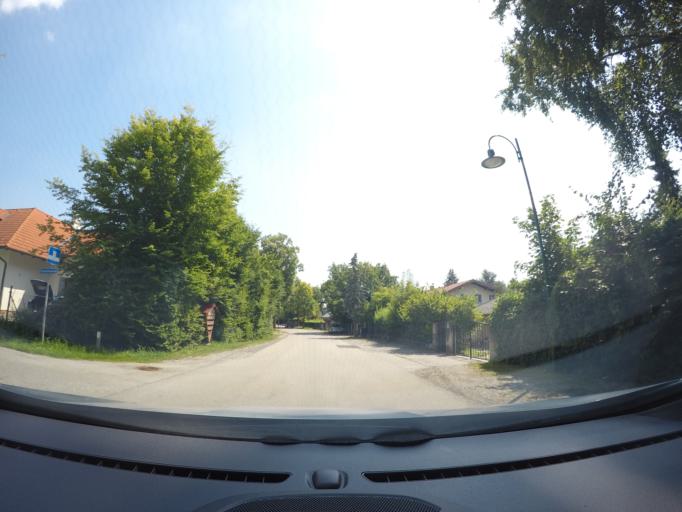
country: AT
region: Lower Austria
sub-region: Politischer Bezirk Tulln
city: Konigstetten
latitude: 48.2731
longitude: 16.1528
